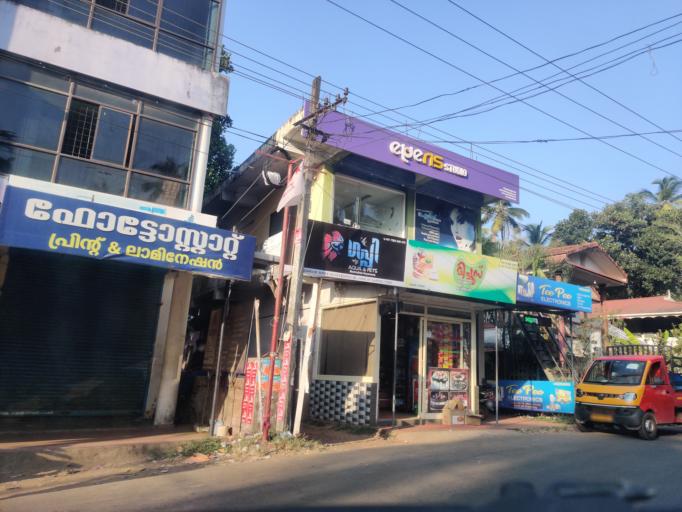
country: IN
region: Kerala
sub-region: Malappuram
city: Ponnani
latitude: 10.7338
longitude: 76.0130
